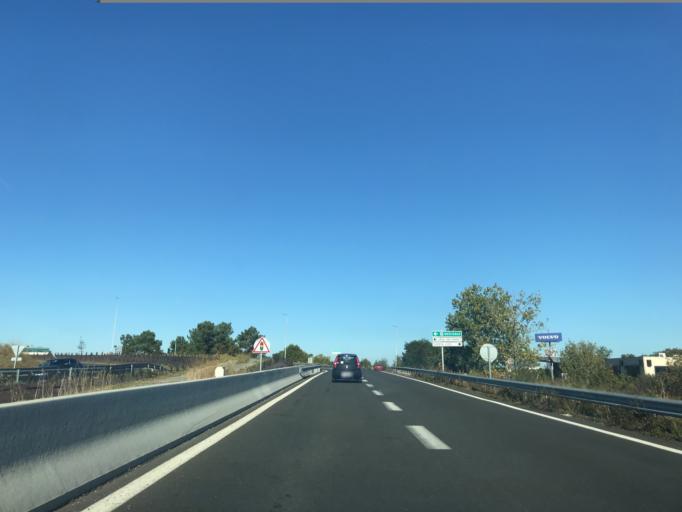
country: FR
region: Aquitaine
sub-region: Departement de la Gironde
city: Pessac
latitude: 44.8309
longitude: -0.6751
